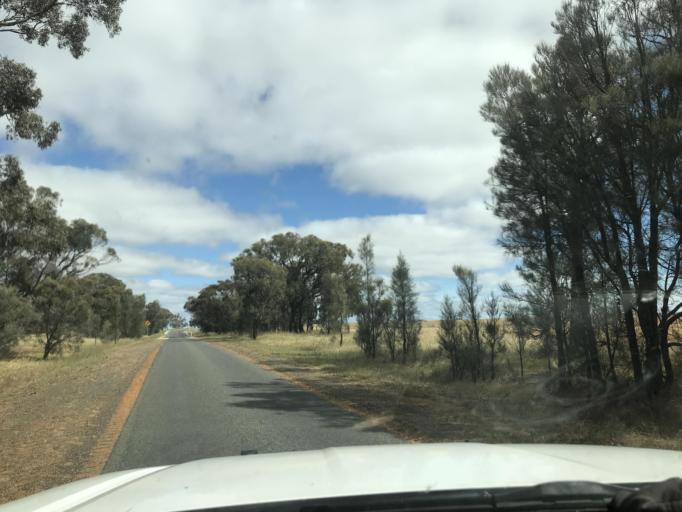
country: AU
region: South Australia
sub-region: Tatiara
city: Bordertown
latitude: -36.3424
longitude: 141.0896
